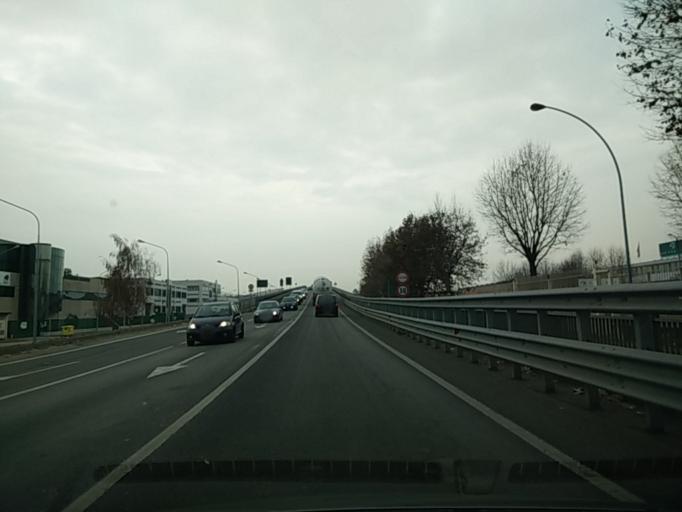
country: IT
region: Piedmont
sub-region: Provincia di Torino
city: Settimo Torinese
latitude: 45.1317
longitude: 7.7345
